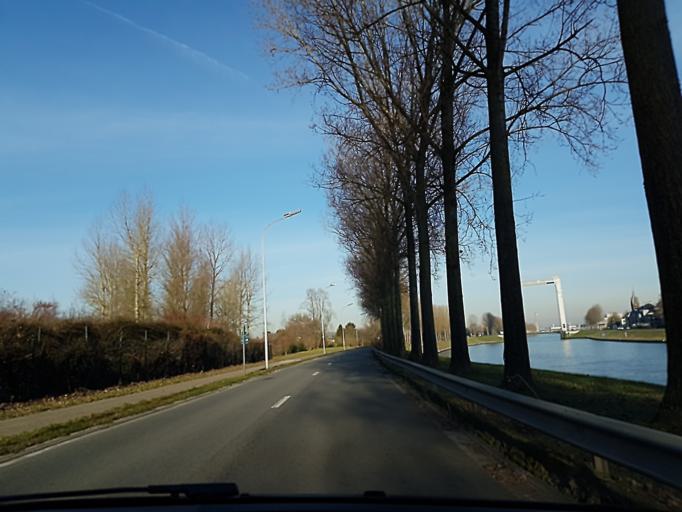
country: BE
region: Flanders
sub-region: Provincie Vlaams-Brabant
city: Kapelle-op-den-Bos
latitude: 51.0295
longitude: 4.3566
